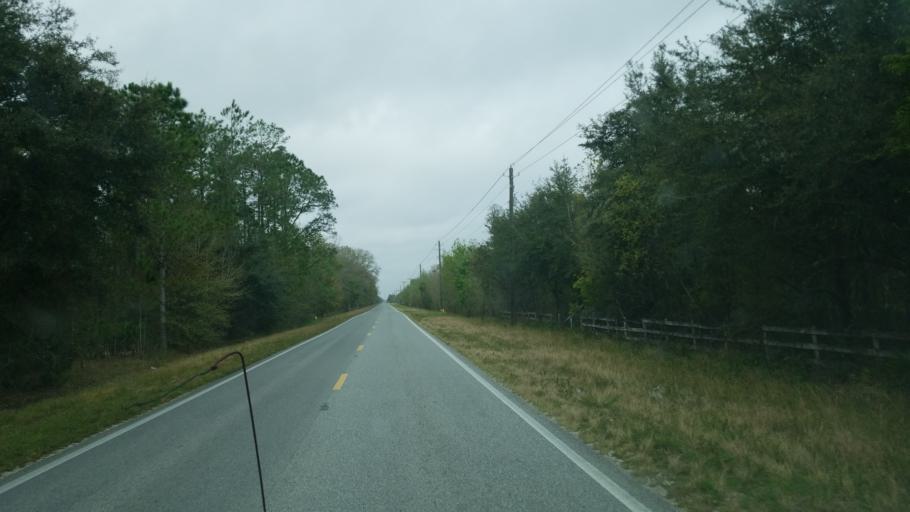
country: US
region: Florida
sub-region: Polk County
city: Polk City
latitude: 28.2590
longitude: -81.8985
